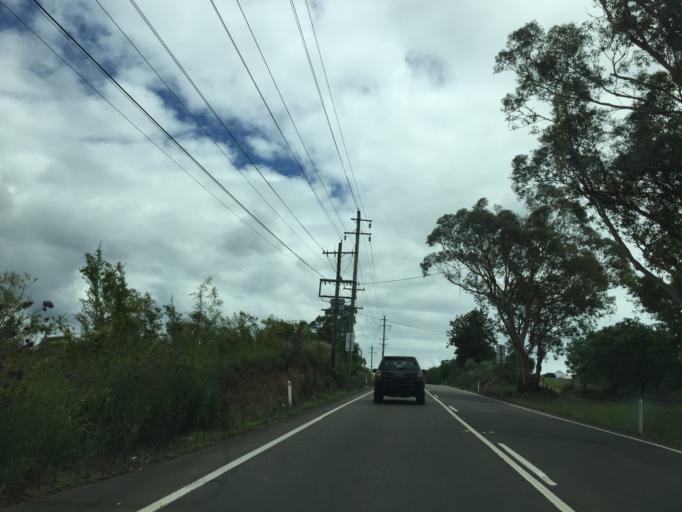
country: AU
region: New South Wales
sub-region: Hawkesbury
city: Richmond
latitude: -33.5654
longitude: 150.7037
